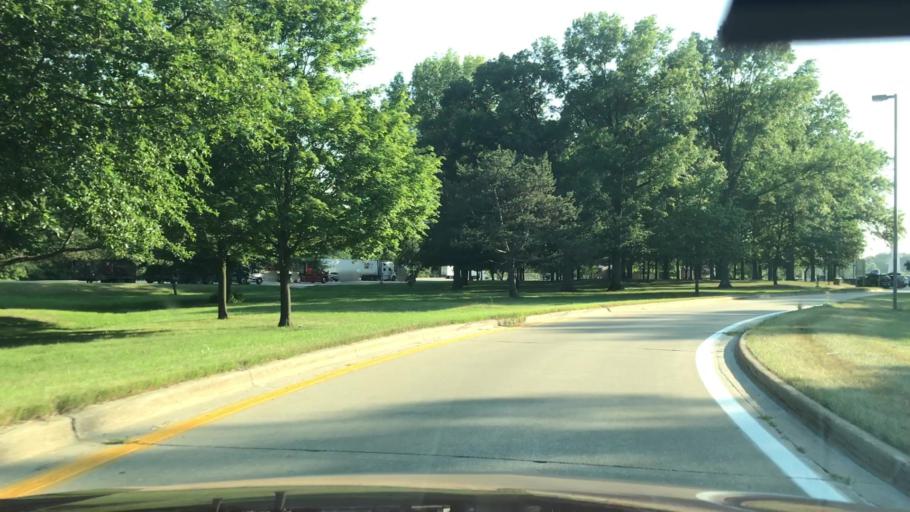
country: US
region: Michigan
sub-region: Berrien County
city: New Buffalo
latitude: 41.7661
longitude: -86.7384
